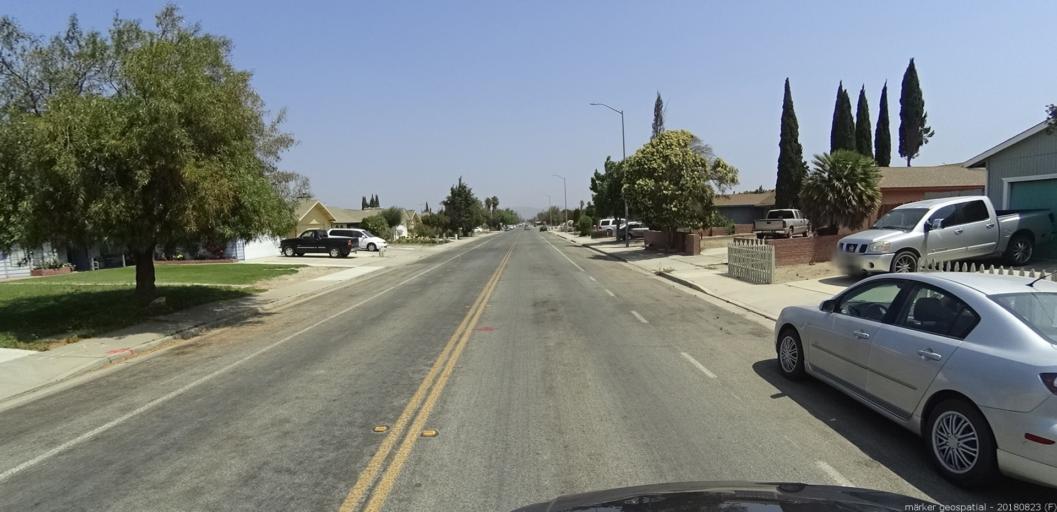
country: US
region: California
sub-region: Monterey County
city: Greenfield
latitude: 36.3202
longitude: -121.2524
